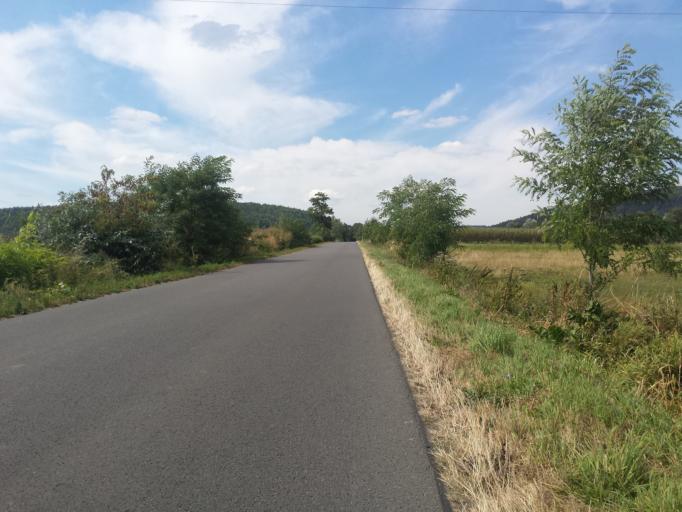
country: PL
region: Subcarpathian Voivodeship
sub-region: Powiat przemyski
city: Fredropol
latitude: 49.6722
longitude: 22.7423
